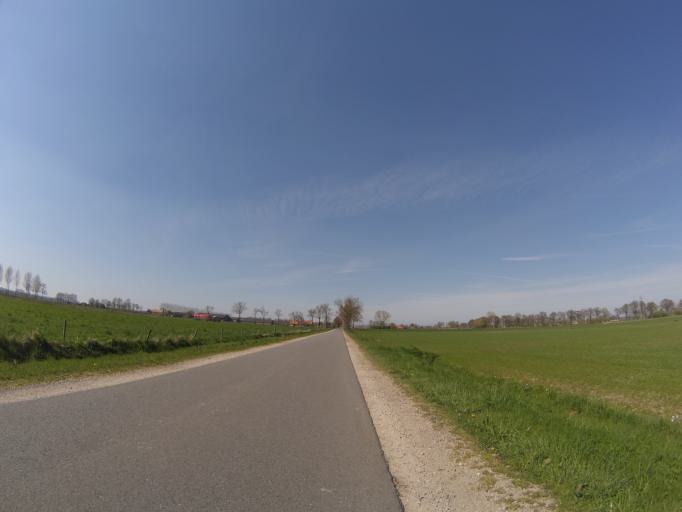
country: NL
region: Gelderland
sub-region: Gemeente Ede
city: Ede
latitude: 51.9983
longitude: 5.6155
